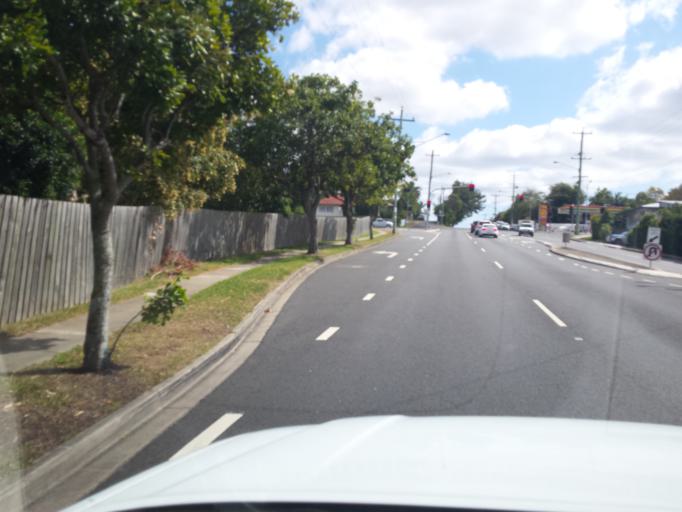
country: AU
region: Queensland
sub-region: Brisbane
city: Zillmere
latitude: -27.3677
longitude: 153.0366
